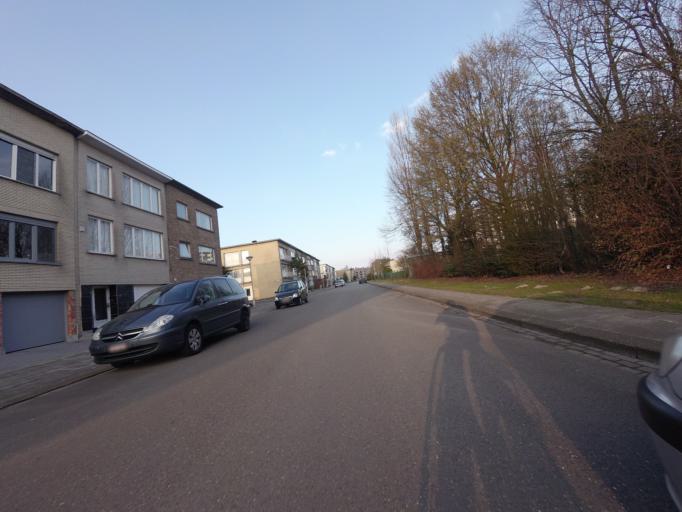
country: BE
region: Flanders
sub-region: Provincie Antwerpen
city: Kapellen
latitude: 51.2718
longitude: 4.4097
